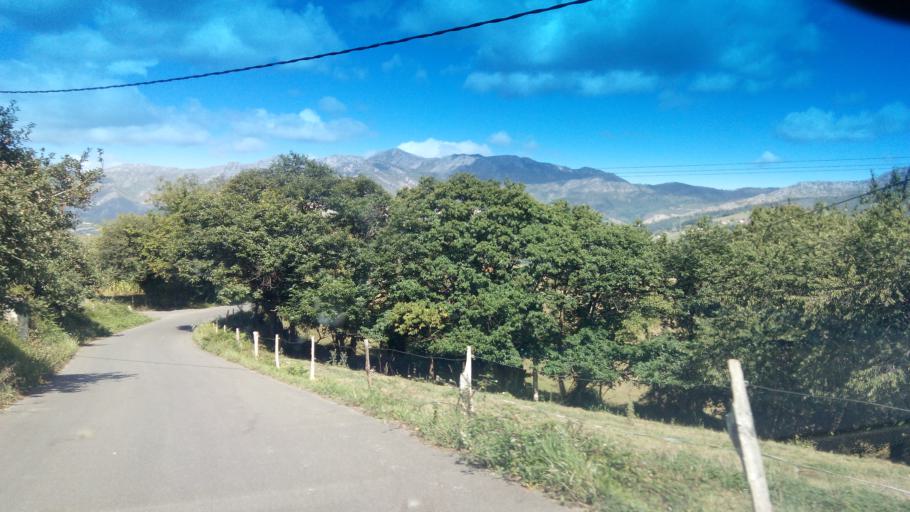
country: ES
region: Asturias
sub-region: Province of Asturias
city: Parres
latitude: 43.3772
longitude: -5.1763
